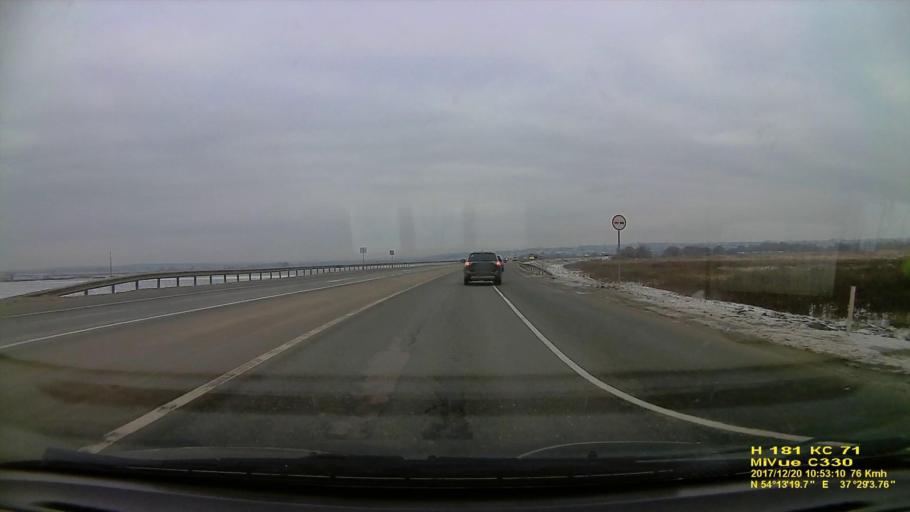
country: RU
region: Tula
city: Barsuki
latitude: 54.2223
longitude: 37.4844
